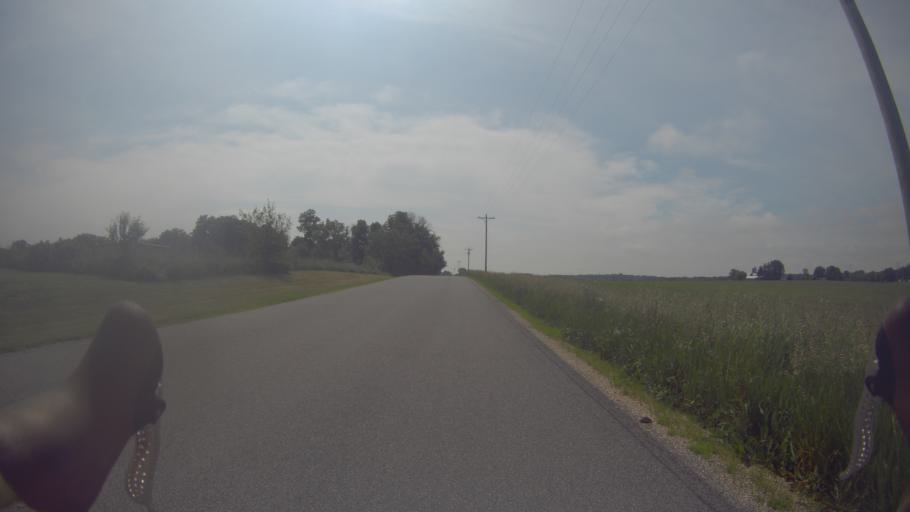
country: US
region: Wisconsin
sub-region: Rock County
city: Edgerton
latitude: 42.8585
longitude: -89.0447
